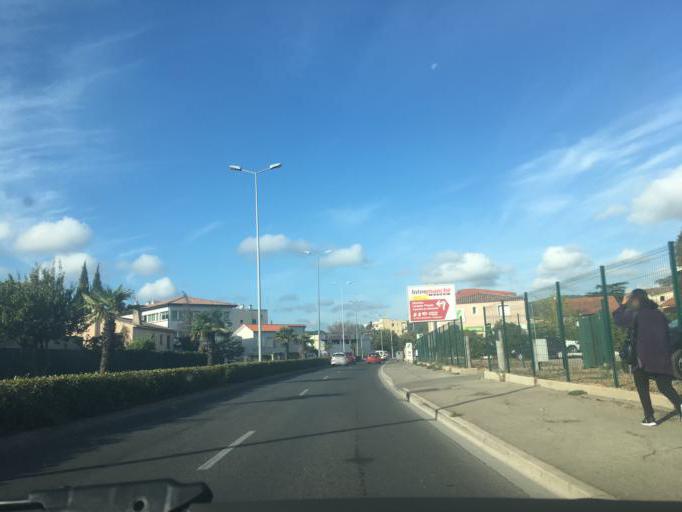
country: FR
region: Provence-Alpes-Cote d'Azur
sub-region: Departement du Var
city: Draguignan
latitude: 43.5344
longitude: 6.4602
